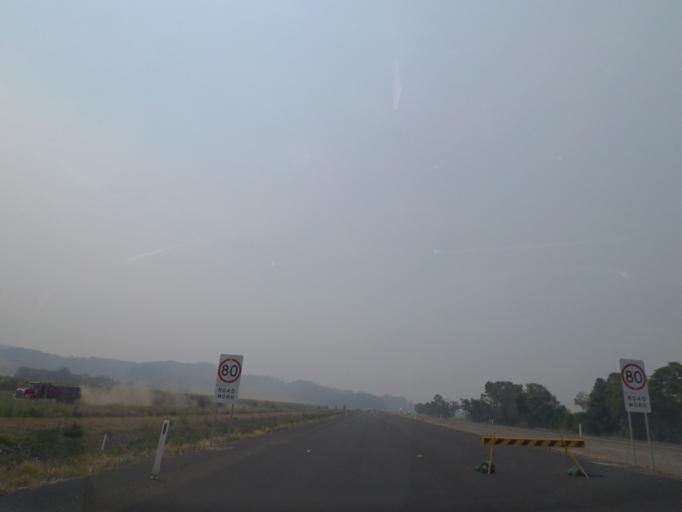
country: AU
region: New South Wales
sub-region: Ballina
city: Ballina
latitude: -28.8908
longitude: 153.4820
